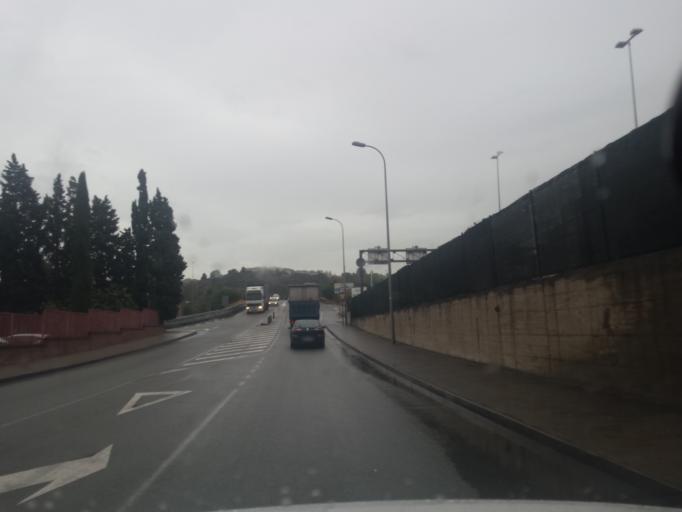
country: ES
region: Catalonia
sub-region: Provincia de Barcelona
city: Castellbisbal
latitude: 41.4650
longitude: 1.9667
